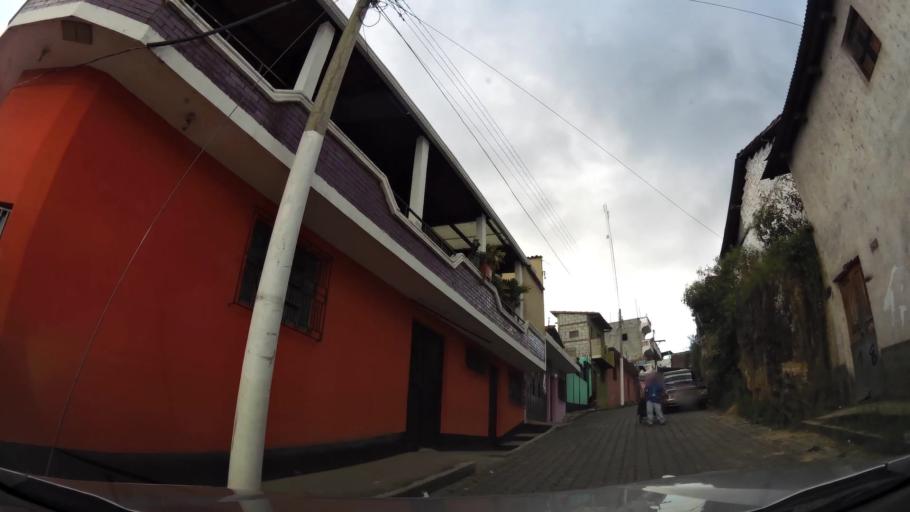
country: GT
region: Quiche
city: Chichicastenango
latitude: 14.9449
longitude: -91.1128
